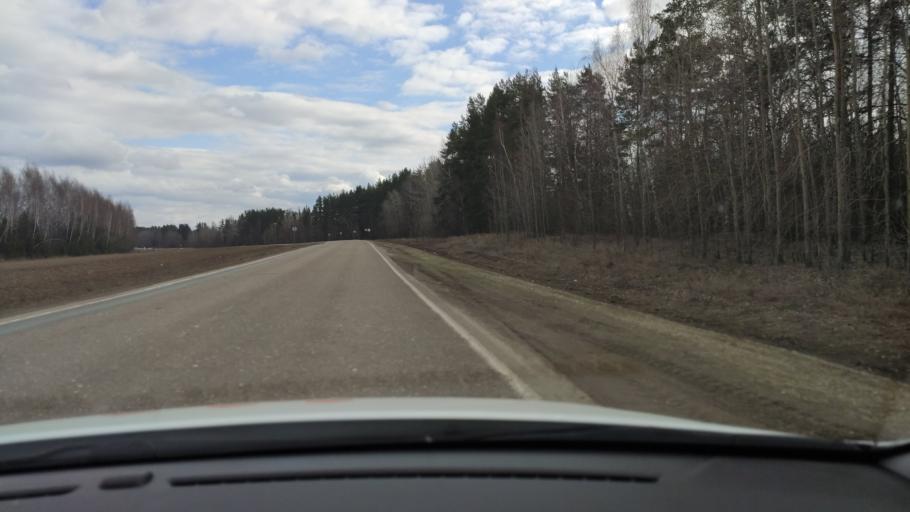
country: RU
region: Tatarstan
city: Vysokaya Gora
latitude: 56.0694
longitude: 49.1956
